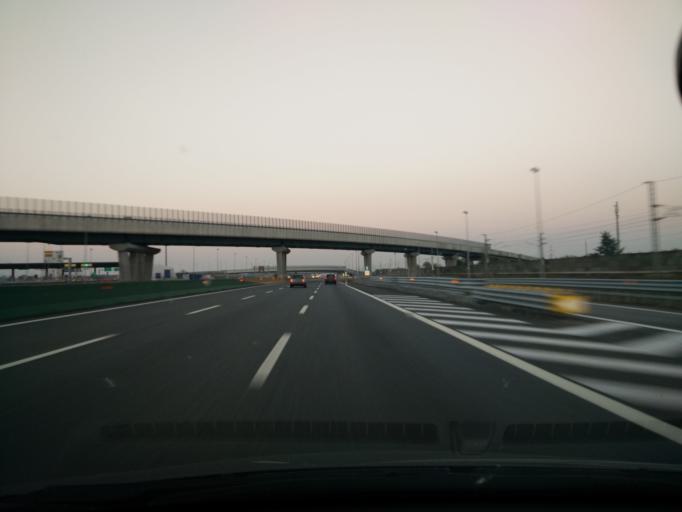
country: IT
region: Piedmont
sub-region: Provincia di Vercelli
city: Borgo d'Ale
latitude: 45.3194
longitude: 8.0709
